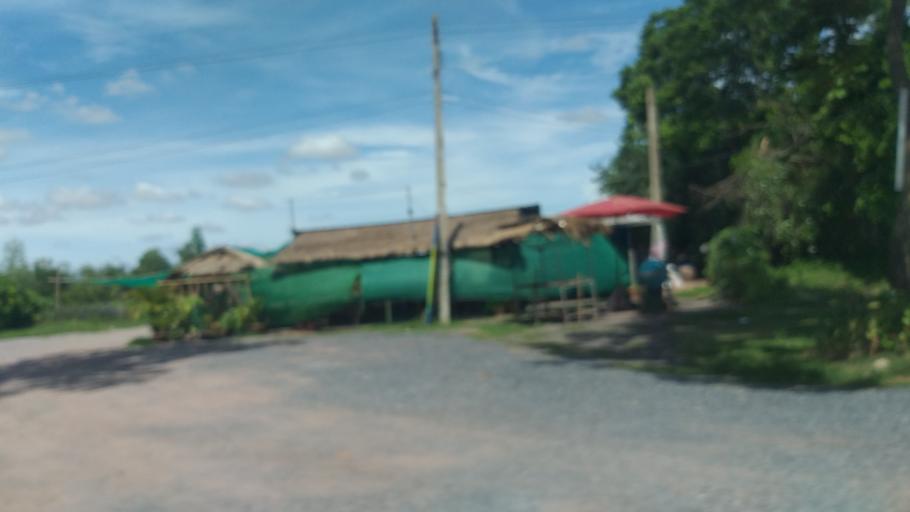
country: TH
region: Khon Kaen
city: Nong Ruea
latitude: 16.4833
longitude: 102.4364
